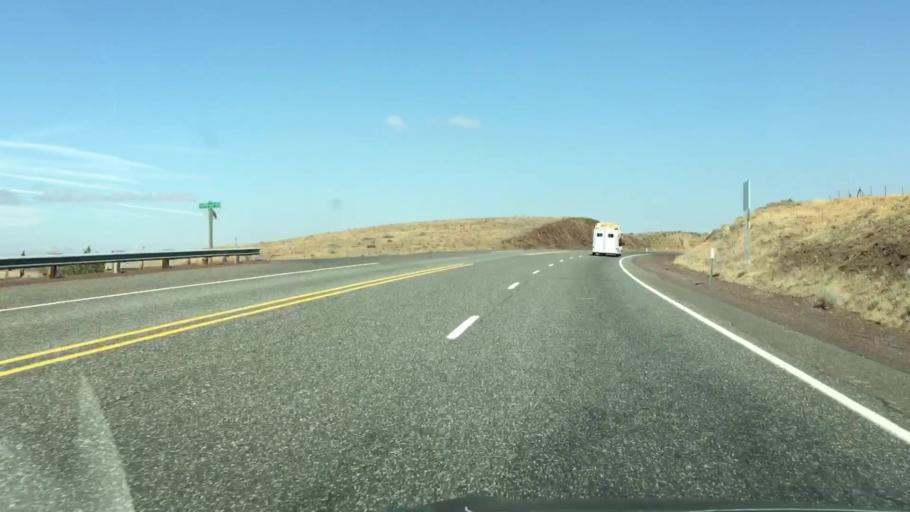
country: US
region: Oregon
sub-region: Wasco County
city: The Dalles
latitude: 45.3192
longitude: -121.1493
